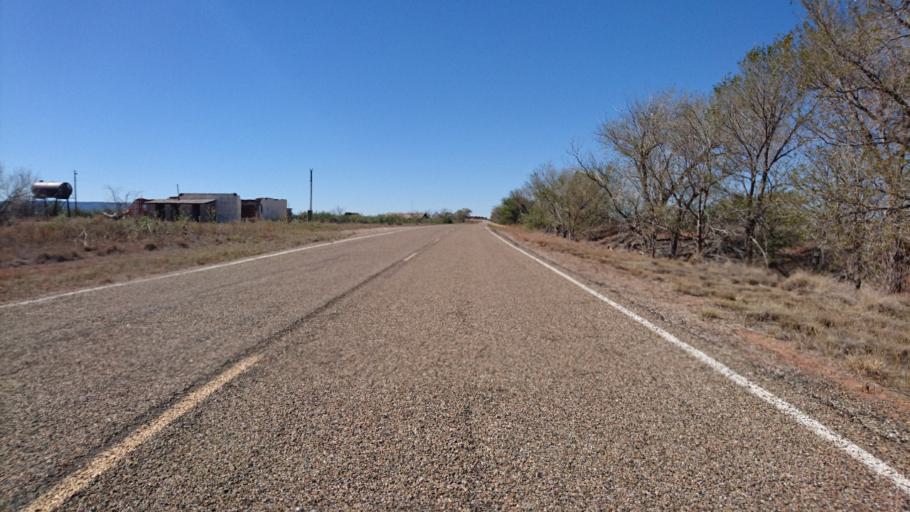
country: US
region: New Mexico
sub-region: Quay County
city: Tucumcari
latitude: 35.0971
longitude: -104.0607
